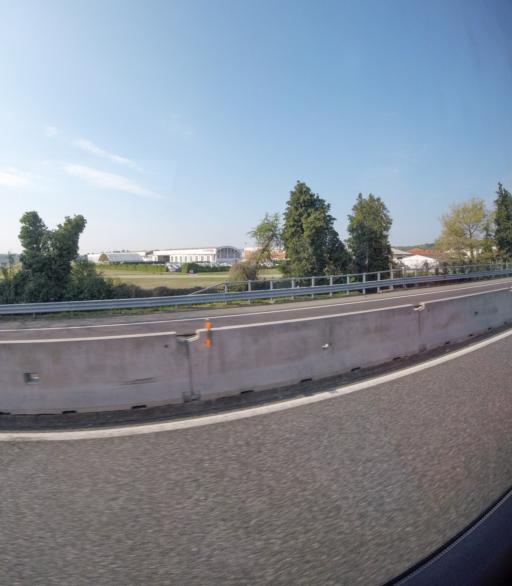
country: IT
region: Lombardy
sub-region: Provincia di Varese
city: Vergiate
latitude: 45.7201
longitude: 8.6964
